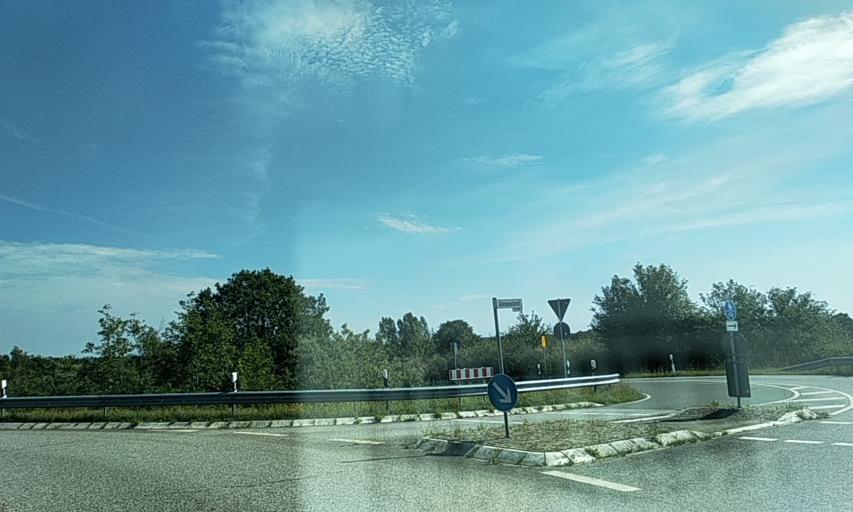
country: DE
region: Schleswig-Holstein
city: Fockbek
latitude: 54.3307
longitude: 9.6239
